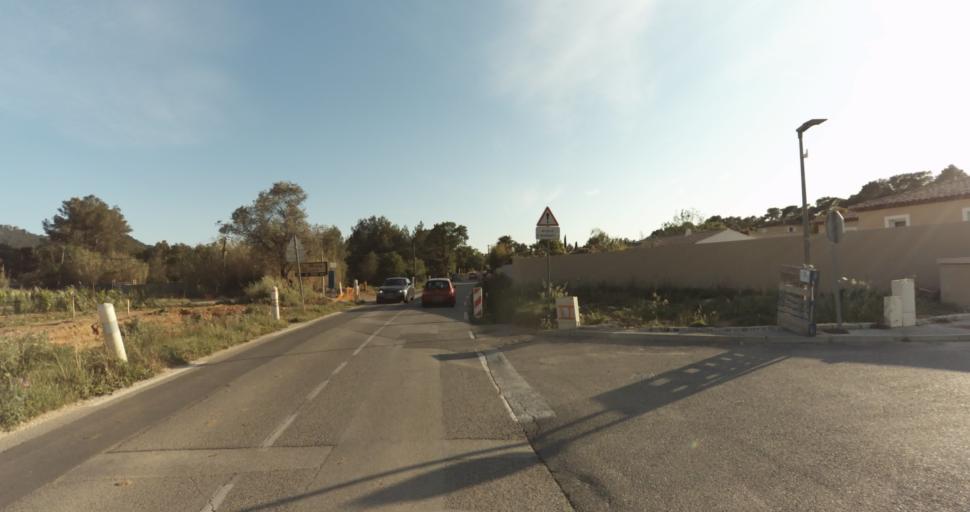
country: FR
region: Provence-Alpes-Cote d'Azur
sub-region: Departement du Var
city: La Crau
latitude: 43.1587
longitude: 6.0971
